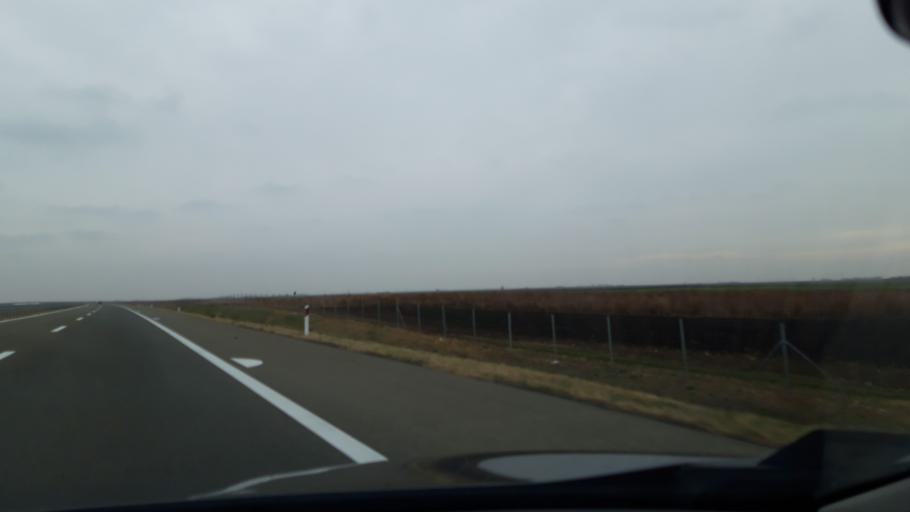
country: RS
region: Autonomna Pokrajina Vojvodina
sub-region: Severnobacki Okrug
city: Backa Topola
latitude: 45.8570
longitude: 19.6979
